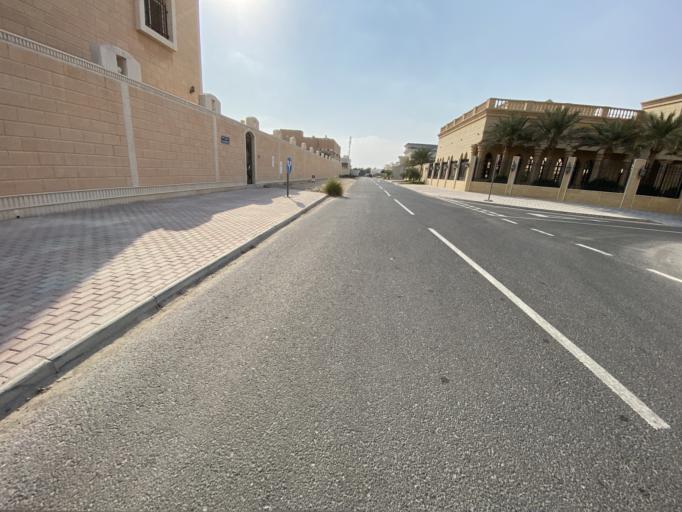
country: QA
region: Baladiyat ar Rayyan
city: Ar Rayyan
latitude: 25.2364
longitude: 51.3776
